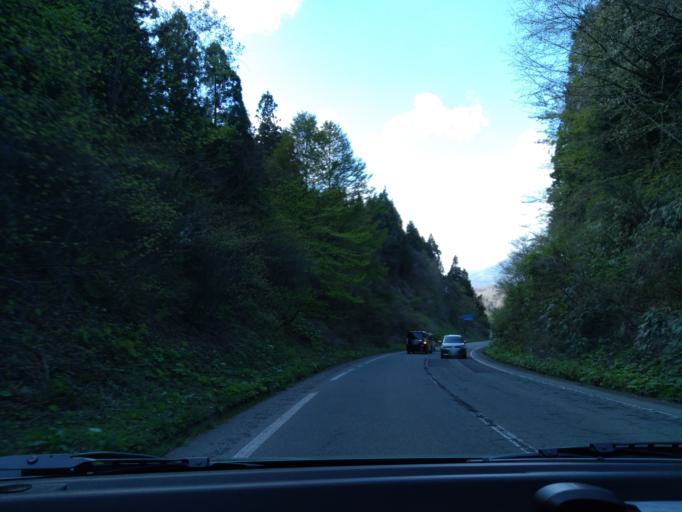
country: JP
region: Akita
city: Akita
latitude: 39.6902
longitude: 140.2749
